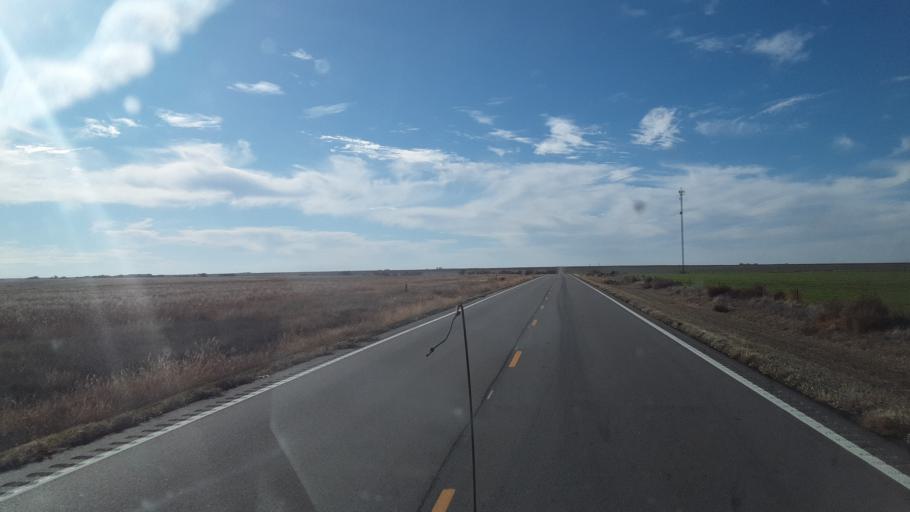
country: US
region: Kansas
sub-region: Hodgeman County
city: Jetmore
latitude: 38.0738
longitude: -100.1648
